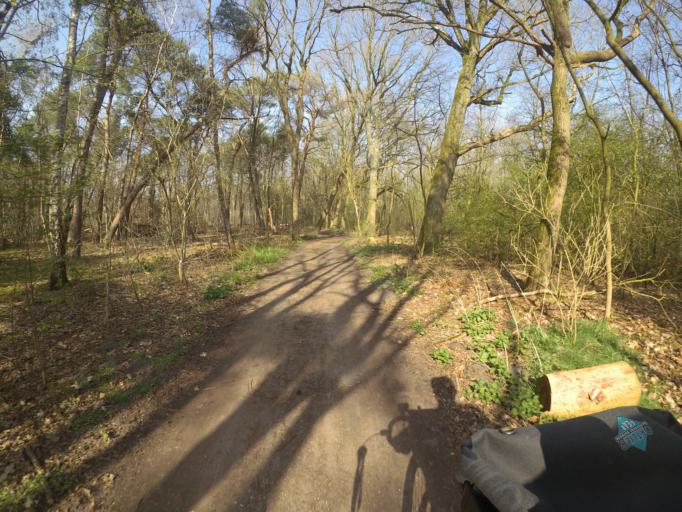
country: NL
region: North Brabant
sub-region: Gemeente Maasdonk
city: Geffen
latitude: 51.6935
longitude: 5.4385
